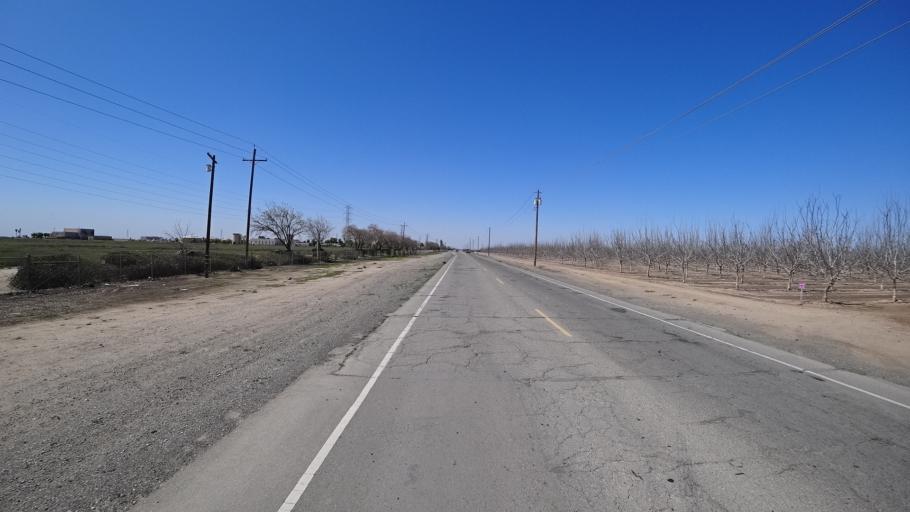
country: US
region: California
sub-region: Fresno County
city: West Park
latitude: 36.7064
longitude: -119.8850
